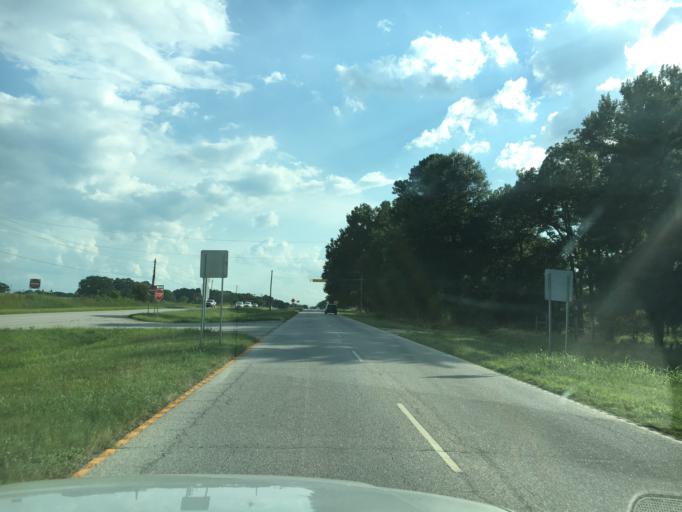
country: US
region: South Carolina
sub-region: Greenwood County
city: Greenwood
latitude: 34.2613
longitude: -82.0863
